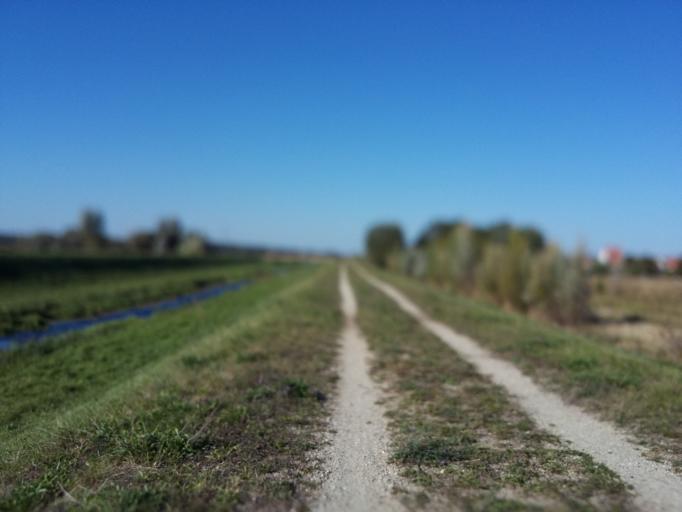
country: AT
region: Lower Austria
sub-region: Politischer Bezirk Ganserndorf
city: Marchegg
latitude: 48.3135
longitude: 16.9717
